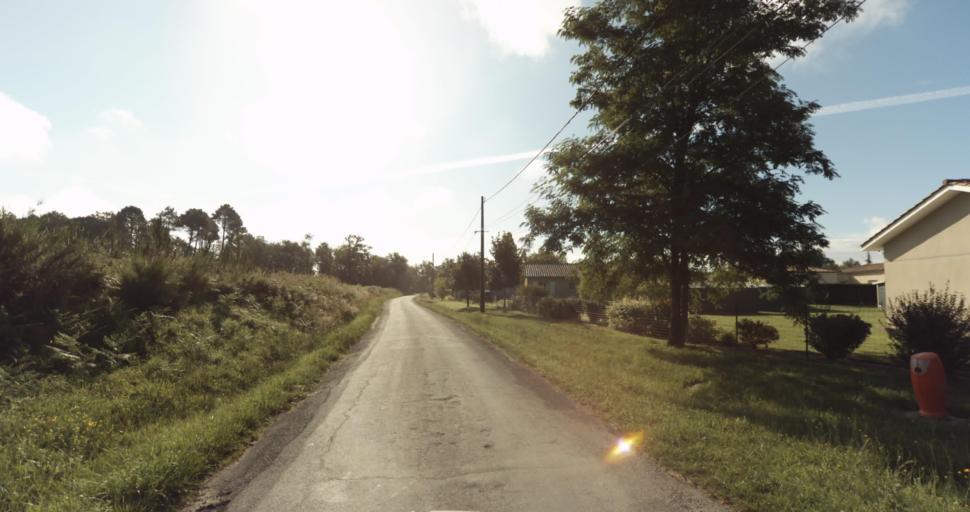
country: FR
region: Aquitaine
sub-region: Departement de la Gironde
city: Bazas
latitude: 44.4398
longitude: -0.2527
